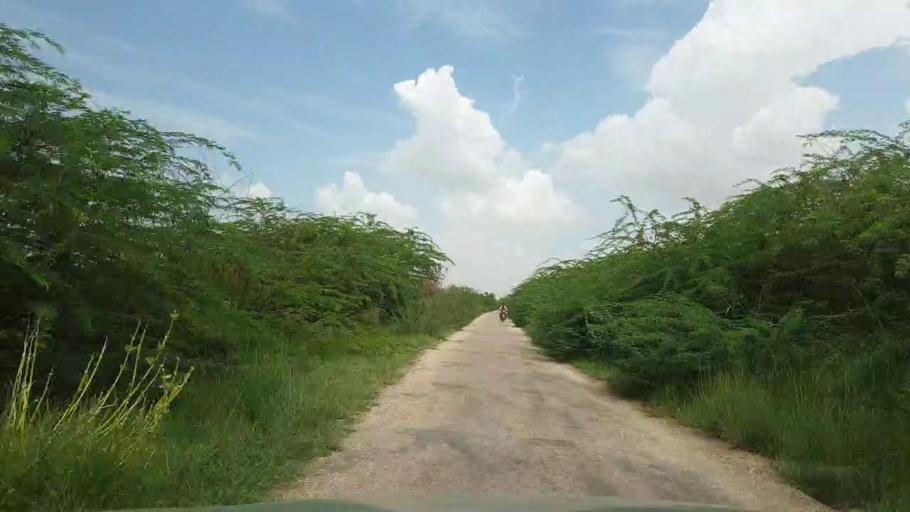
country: PK
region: Sindh
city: Bozdar
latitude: 27.0253
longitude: 68.9516
